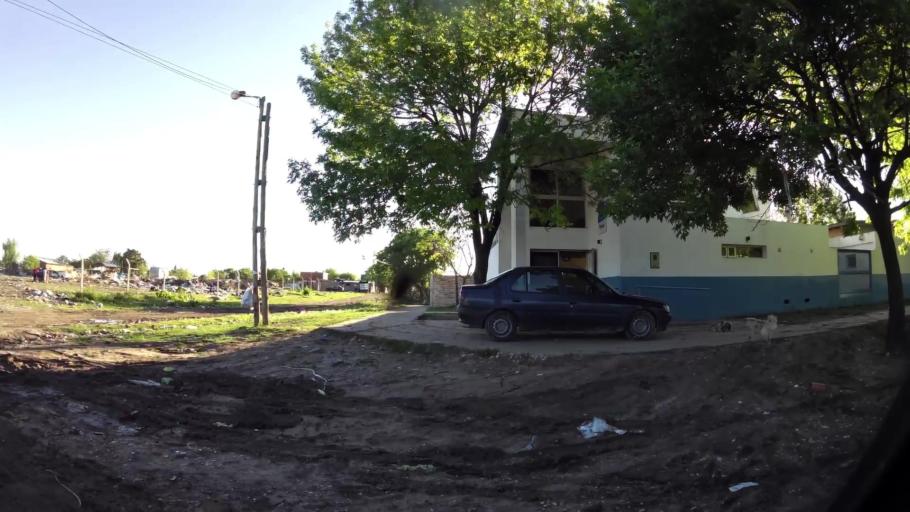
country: AR
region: Buenos Aires
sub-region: Partido de Almirante Brown
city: Adrogue
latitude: -34.7744
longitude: -58.3409
